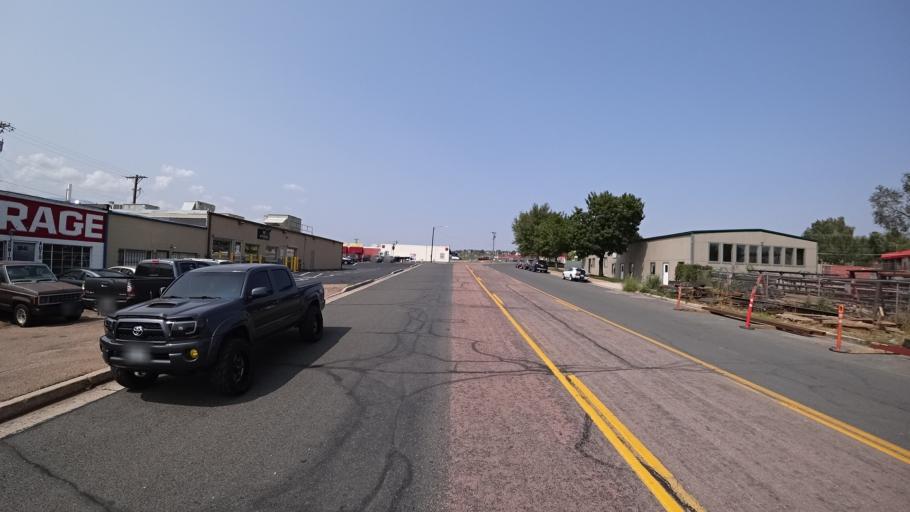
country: US
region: Colorado
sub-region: El Paso County
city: Stratmoor
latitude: 38.7953
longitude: -104.7768
